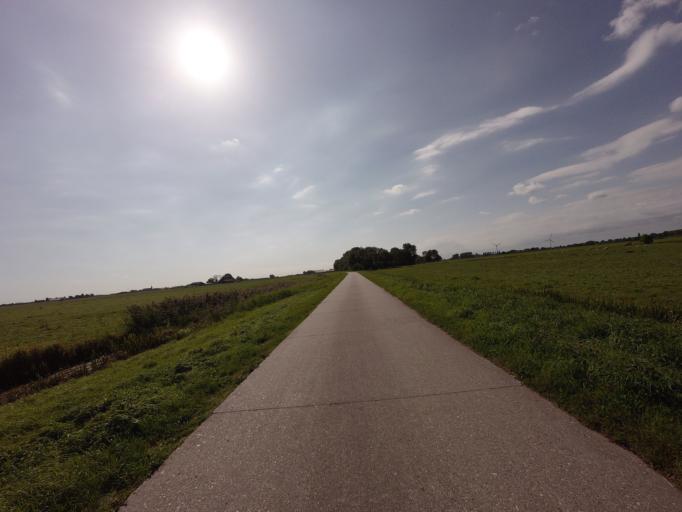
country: NL
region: Friesland
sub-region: Gemeente Littenseradiel
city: Makkum
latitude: 53.0951
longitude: 5.6455
